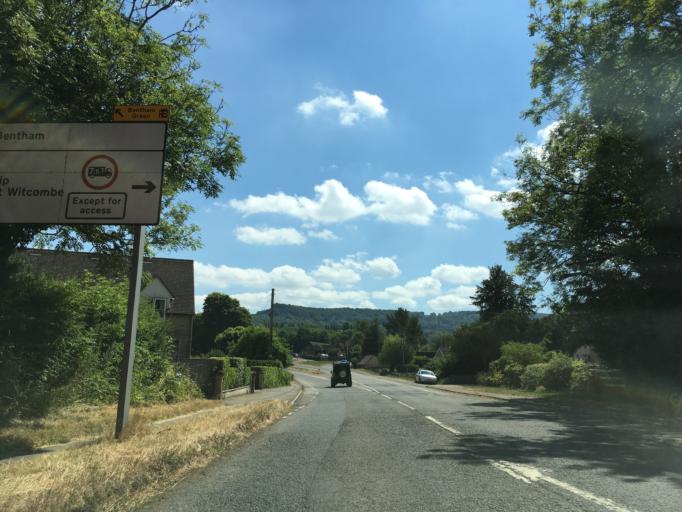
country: GB
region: England
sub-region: Gloucestershire
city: Shurdington
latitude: 51.8404
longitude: -2.1431
